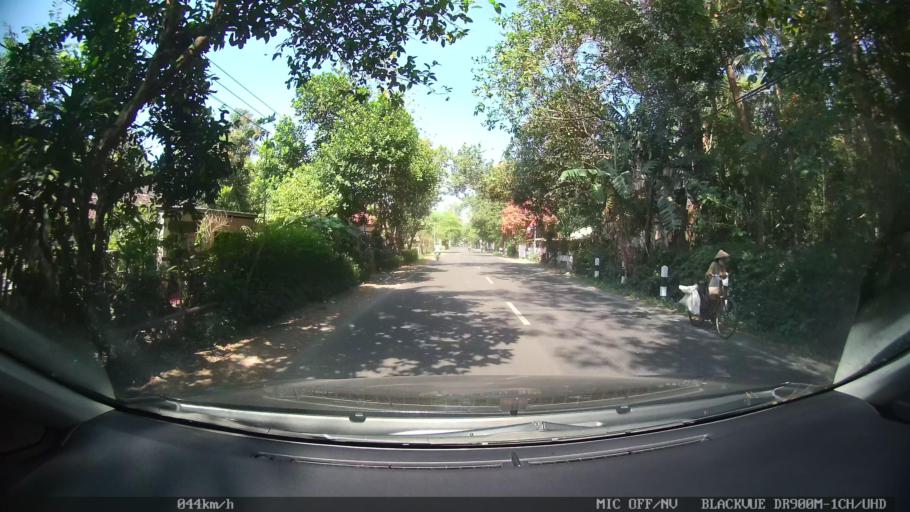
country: ID
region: Daerah Istimewa Yogyakarta
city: Srandakan
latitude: -7.9413
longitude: 110.2326
